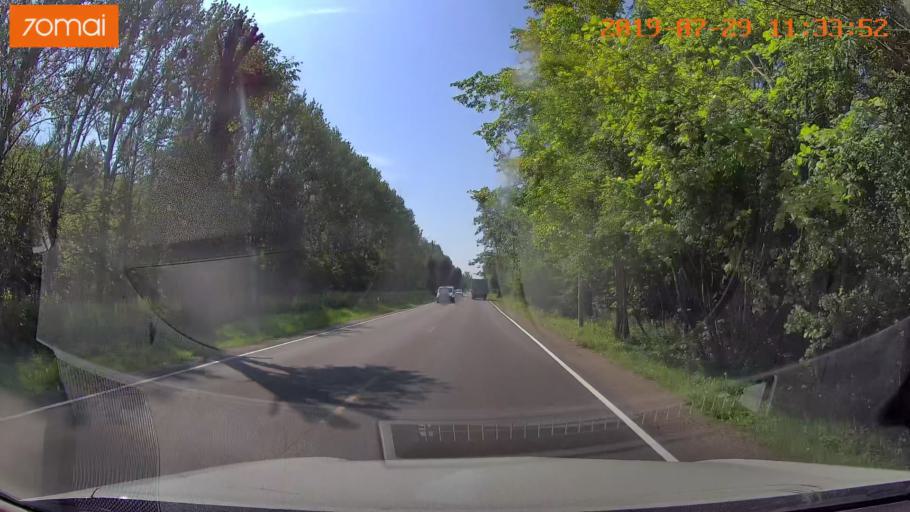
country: RU
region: Kaliningrad
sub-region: Gorod Kaliningrad
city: Kaliningrad
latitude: 54.6609
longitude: 20.5410
